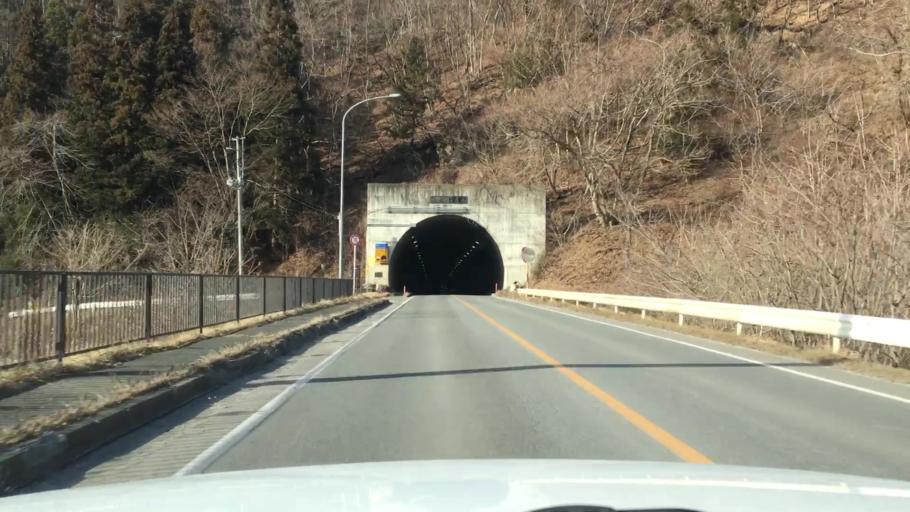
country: JP
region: Iwate
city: Tono
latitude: 39.6344
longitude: 141.6028
